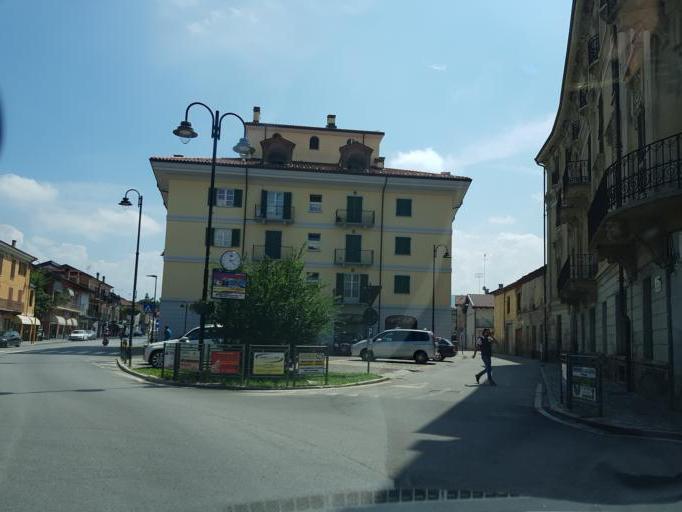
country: IT
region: Piedmont
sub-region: Provincia di Cuneo
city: Caraglio
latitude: 44.4193
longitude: 7.4324
